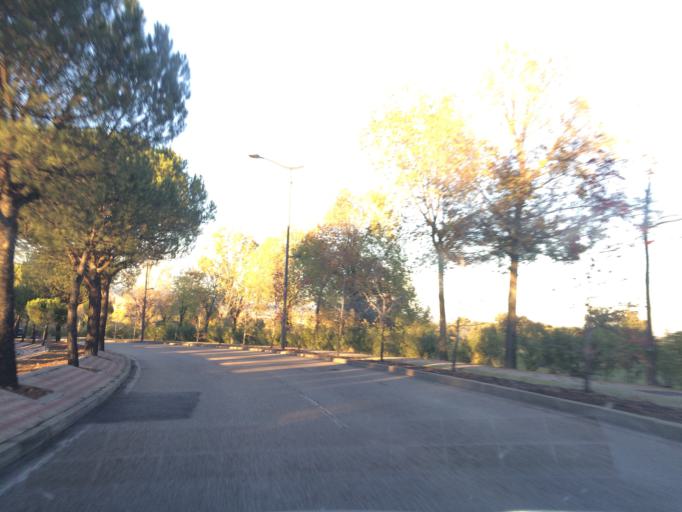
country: ES
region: Madrid
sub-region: Provincia de Madrid
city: Tres Cantos
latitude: 40.5862
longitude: -3.7038
